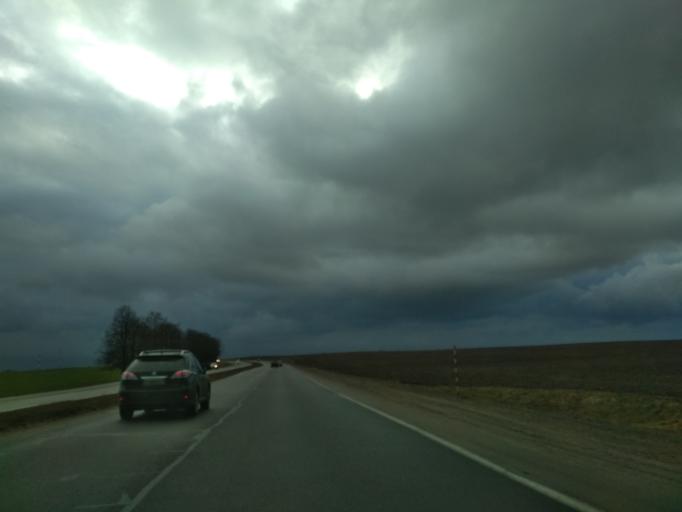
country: BY
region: Minsk
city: Luhavaya Slabada
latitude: 53.7550
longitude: 27.8312
